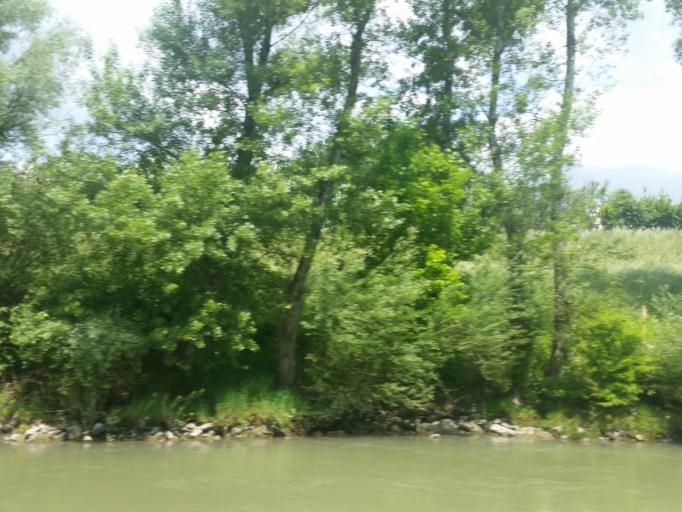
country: AT
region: Lower Austria
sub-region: Politischer Bezirk Wien-Umgebung
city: Schwechat
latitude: 48.1787
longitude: 16.4588
